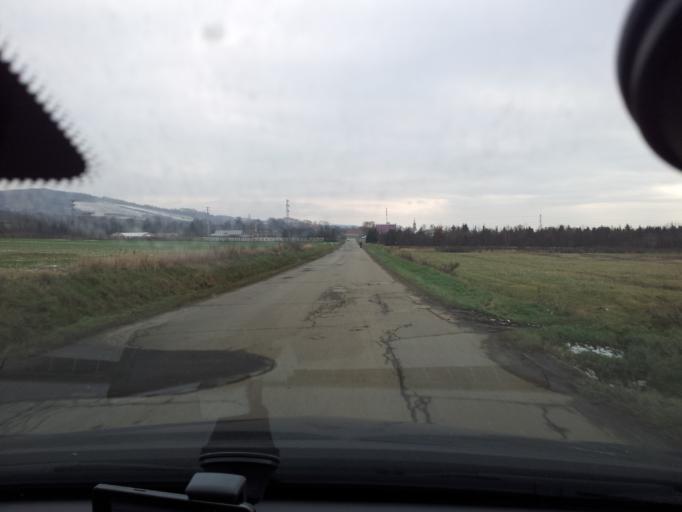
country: SK
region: Kosicky
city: Kosice
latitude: 48.7424
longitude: 21.3454
